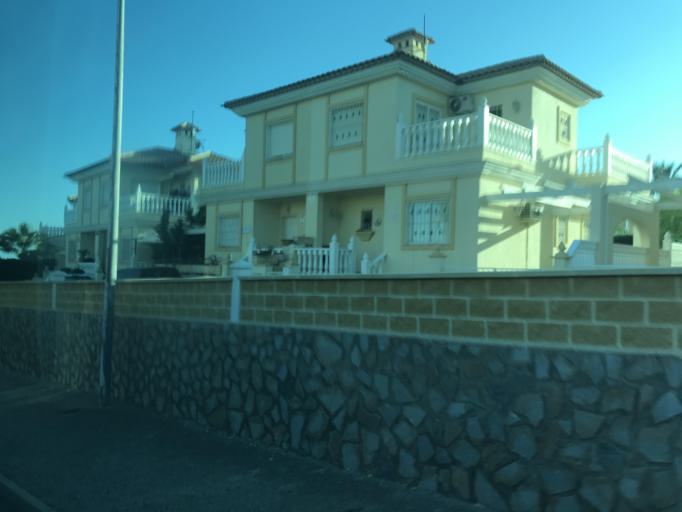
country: ES
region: Valencia
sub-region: Provincia de Alicante
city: Torrevieja
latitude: 38.0016
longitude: -0.6522
